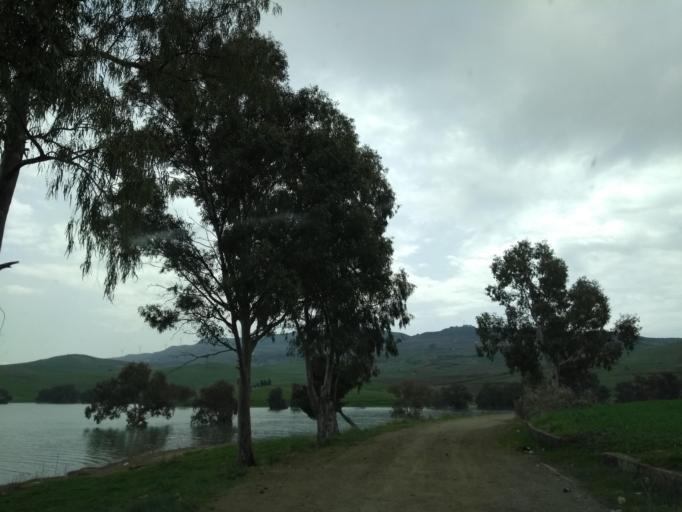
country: IT
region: Sicily
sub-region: Palermo
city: Partinico
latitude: 37.9898
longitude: 13.0830
